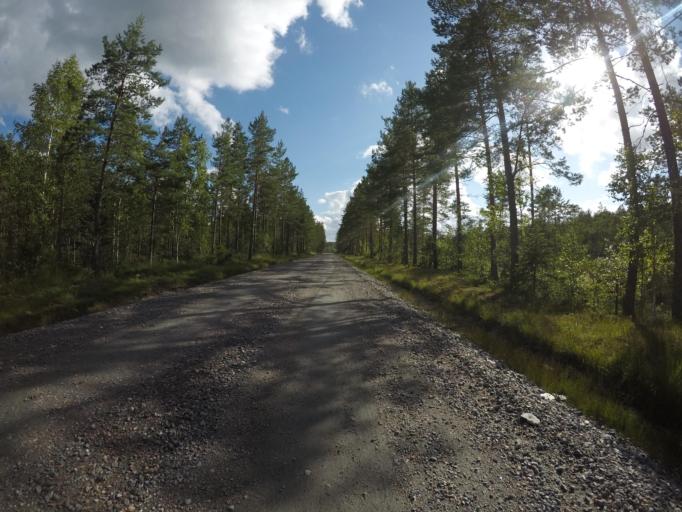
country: SE
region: OErebro
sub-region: Hallefors Kommun
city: Haellefors
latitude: 59.9208
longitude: 14.6005
